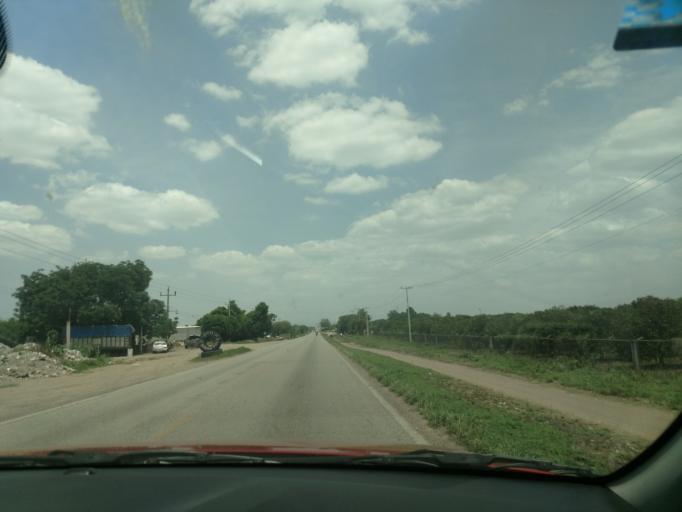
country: MX
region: San Luis Potosi
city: Ciudad Fernandez
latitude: 21.9493
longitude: -100.0601
